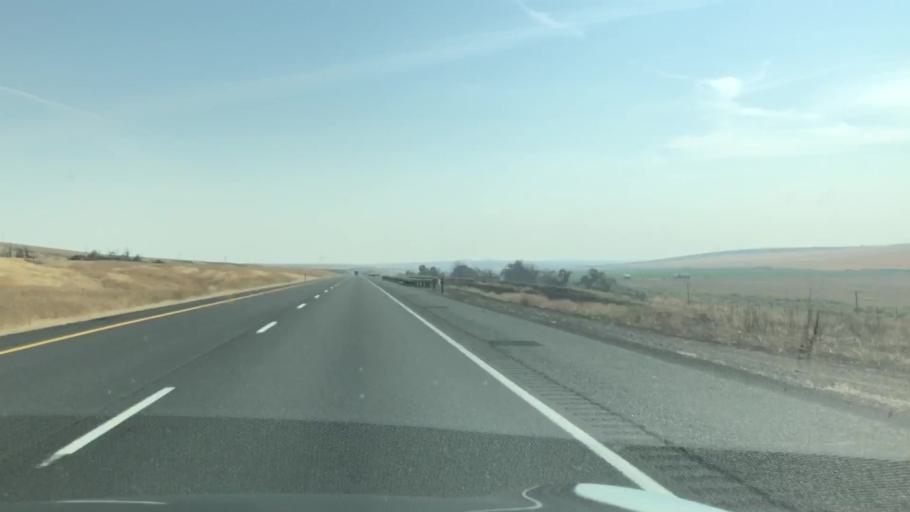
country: US
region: Washington
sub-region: Grant County
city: Warden
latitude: 47.0844
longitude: -118.9501
